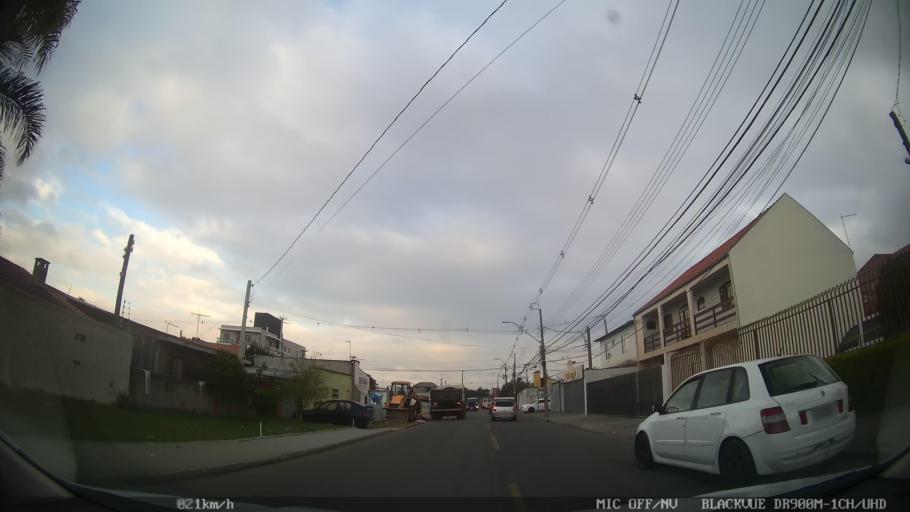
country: BR
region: Parana
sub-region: Pinhais
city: Pinhais
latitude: -25.4320
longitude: -49.1781
